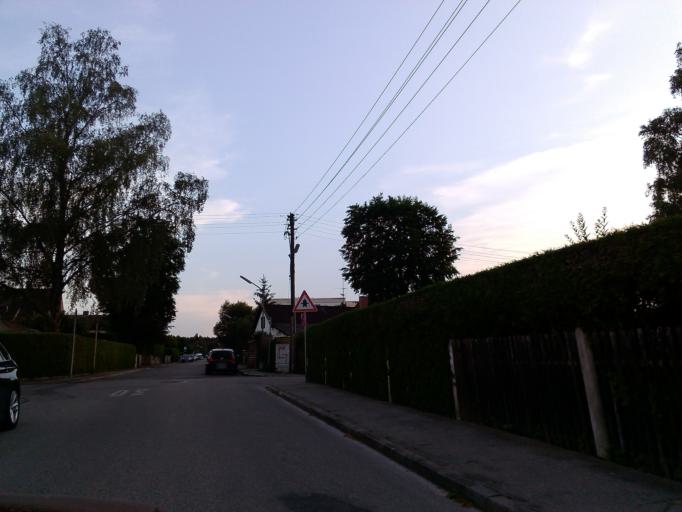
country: DE
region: Bavaria
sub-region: Upper Bavaria
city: Gauting
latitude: 48.0653
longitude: 11.3916
